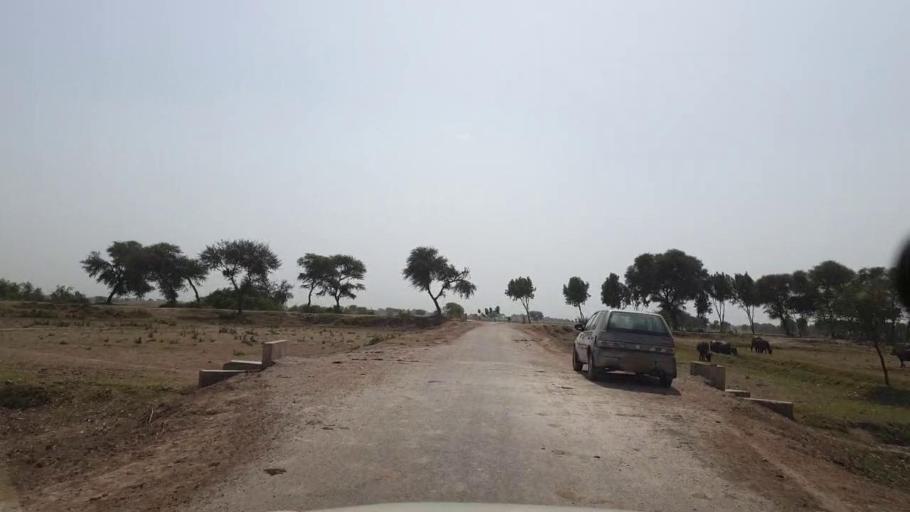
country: PK
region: Sindh
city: Matli
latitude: 25.0514
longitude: 68.6816
